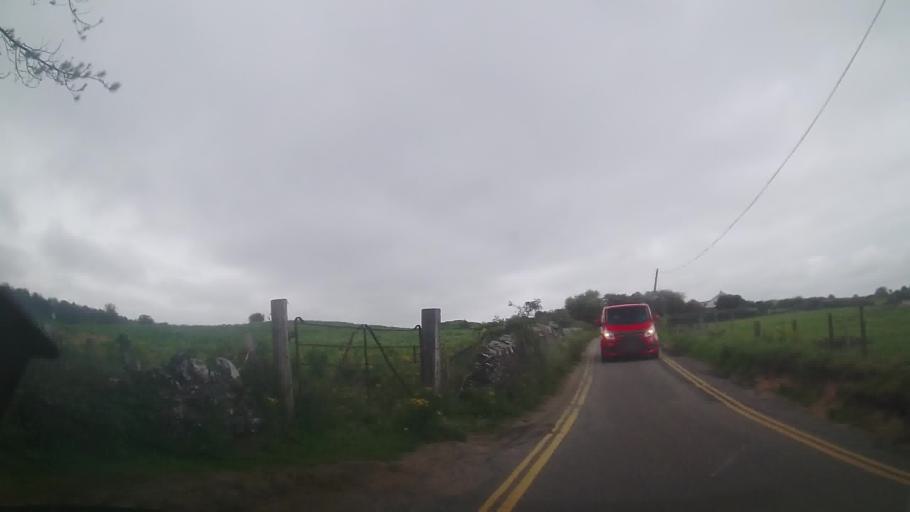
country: GB
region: Wales
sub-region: Gwynedd
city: Caernarfon
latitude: 53.1586
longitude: -4.3722
